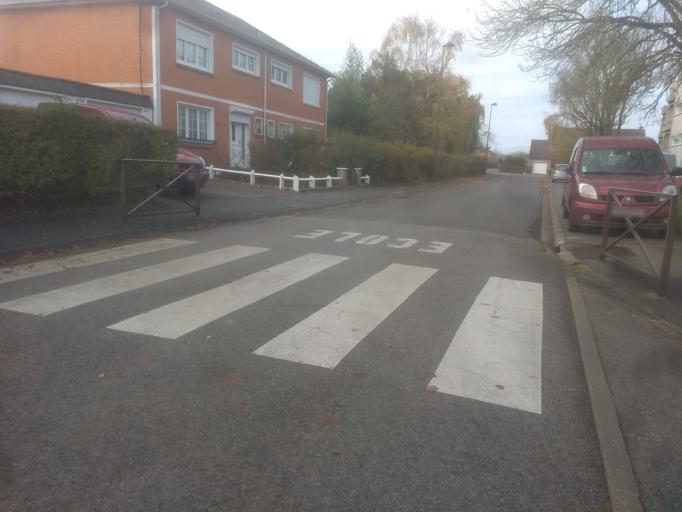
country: FR
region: Nord-Pas-de-Calais
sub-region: Departement du Pas-de-Calais
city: Dainville
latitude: 50.2936
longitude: 2.7306
